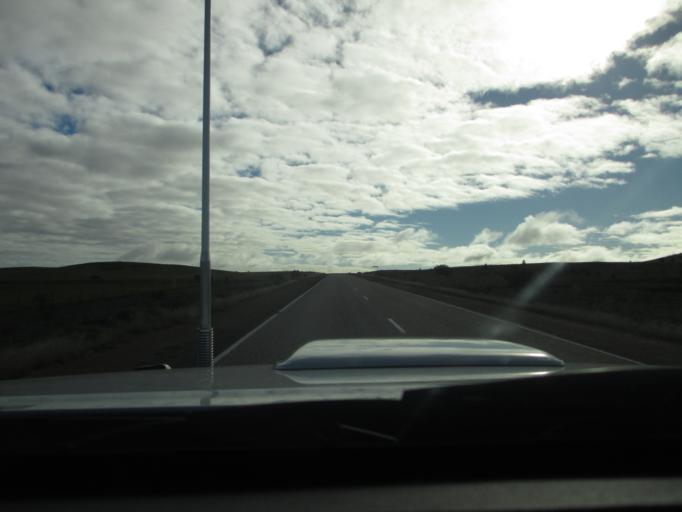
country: AU
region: South Australia
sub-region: Peterborough
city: Peterborough
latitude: -32.5692
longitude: 138.5640
